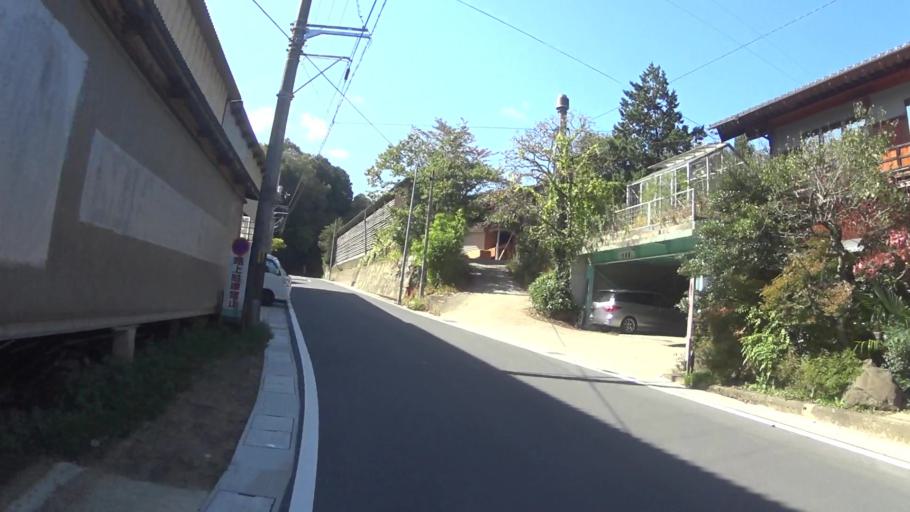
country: JP
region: Hyogo
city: Toyooka
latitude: 35.5933
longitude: 134.9539
